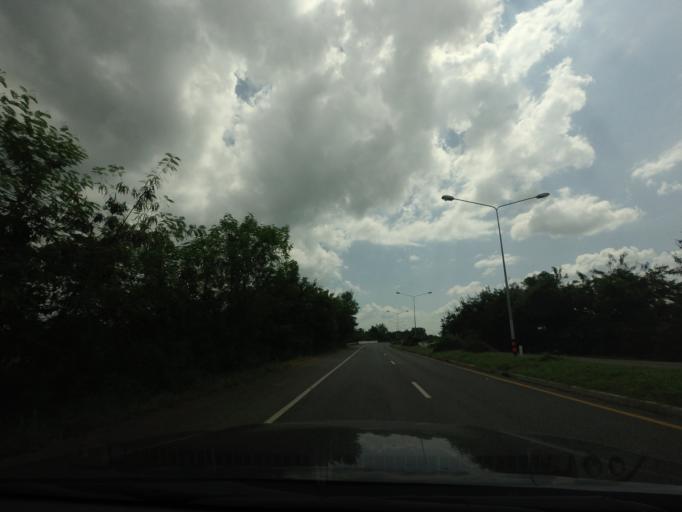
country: TH
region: Phetchabun
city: Nong Phai
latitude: 16.1863
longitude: 101.0889
